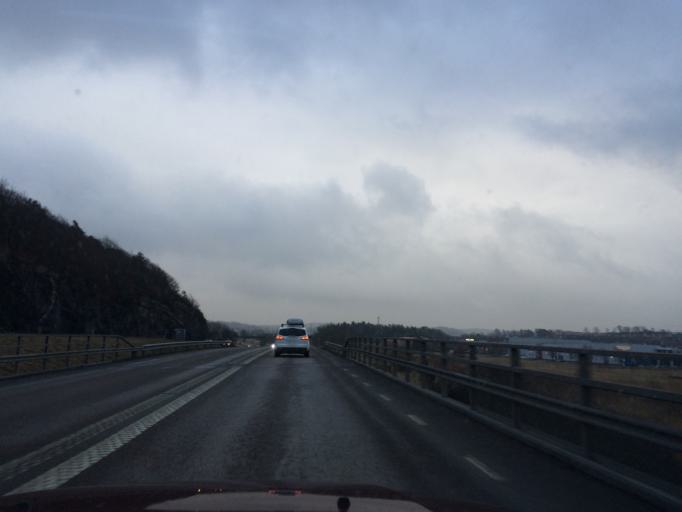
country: SE
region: Halland
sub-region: Kungsbacka Kommun
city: Kungsbacka
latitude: 57.5104
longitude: 12.0523
